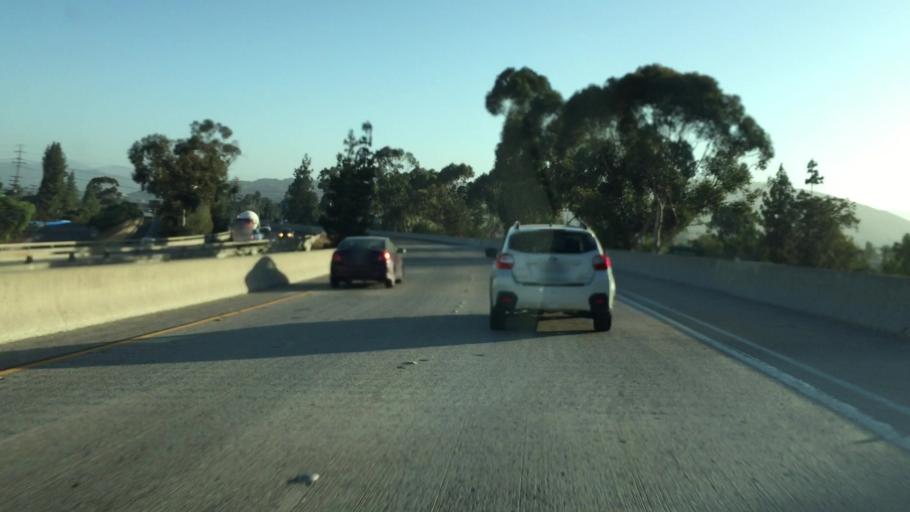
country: US
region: California
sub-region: San Diego County
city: El Cajon
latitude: 32.8049
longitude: -116.9624
